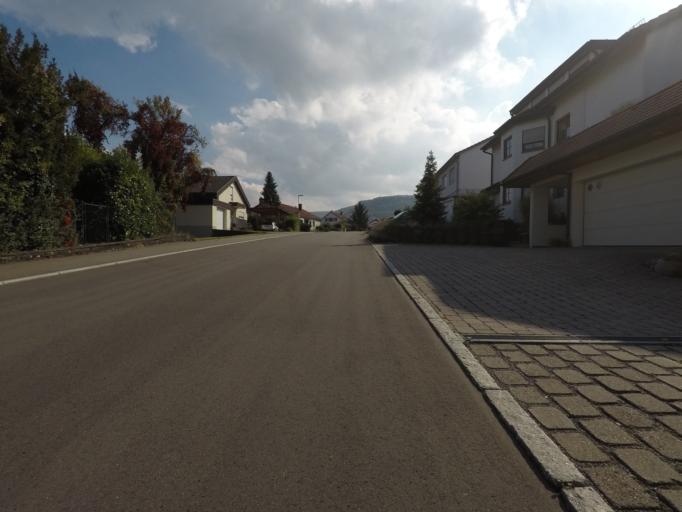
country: DE
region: Baden-Wuerttemberg
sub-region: Tuebingen Region
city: Pfullingen
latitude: 48.4622
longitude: 9.2192
